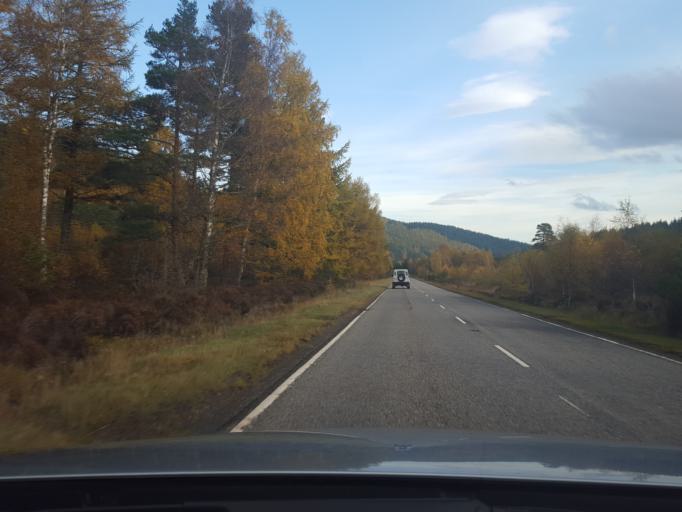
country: GB
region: Scotland
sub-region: Highland
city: Spean Bridge
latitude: 57.1972
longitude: -4.7361
